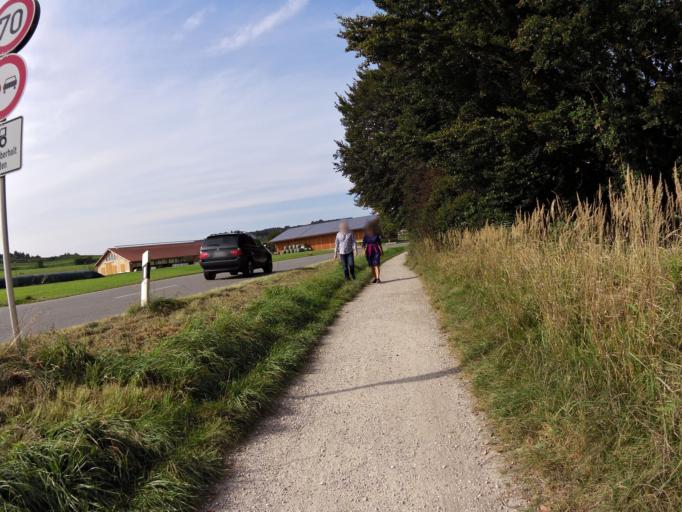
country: DE
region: Bavaria
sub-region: Upper Bavaria
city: Tutzing
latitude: 47.8859
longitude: 11.2695
